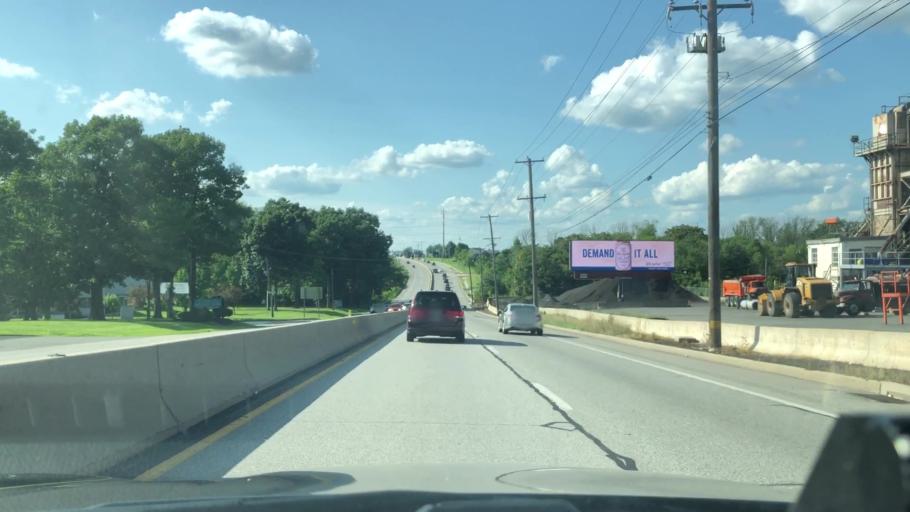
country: US
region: Pennsylvania
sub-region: Montgomery County
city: Montgomeryville
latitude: 40.2199
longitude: -75.2306
